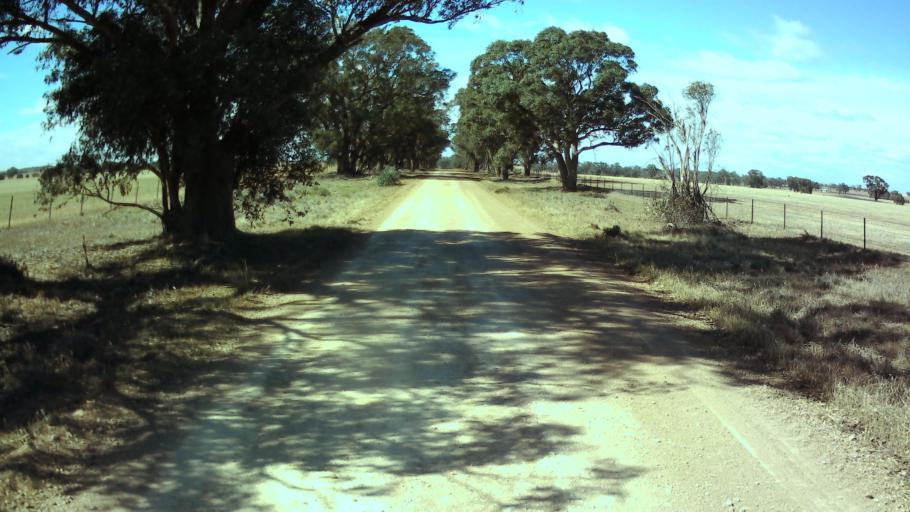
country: AU
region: New South Wales
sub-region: Weddin
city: Grenfell
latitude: -34.0540
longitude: 148.3133
